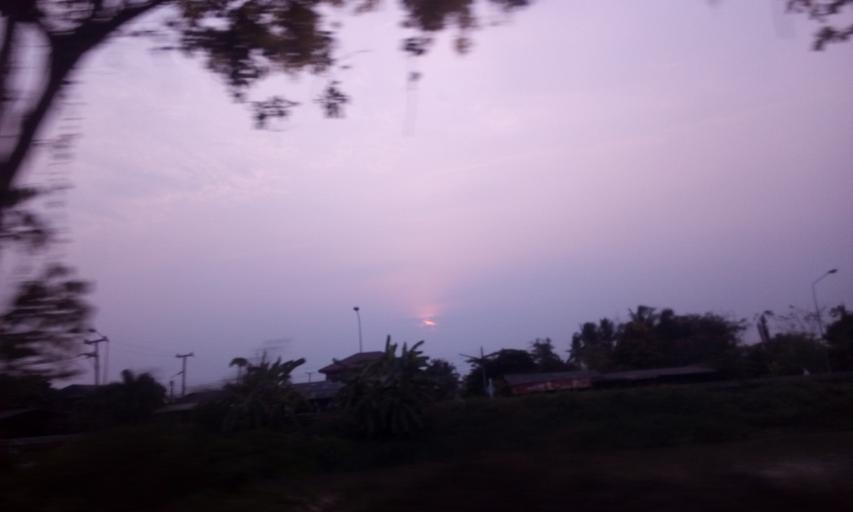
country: TH
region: Pathum Thani
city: Nong Suea
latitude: 14.0404
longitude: 100.8935
